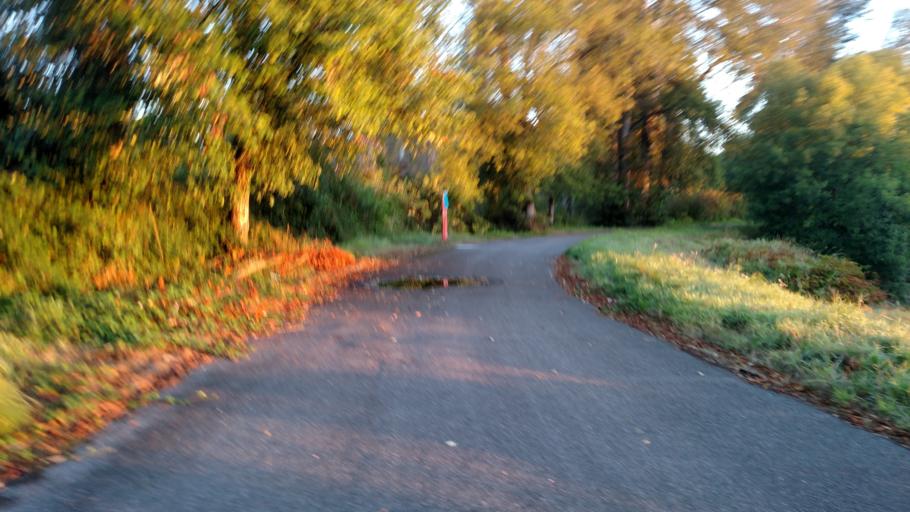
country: US
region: Washington
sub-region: King County
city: Kent
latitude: 47.3885
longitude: -122.2733
